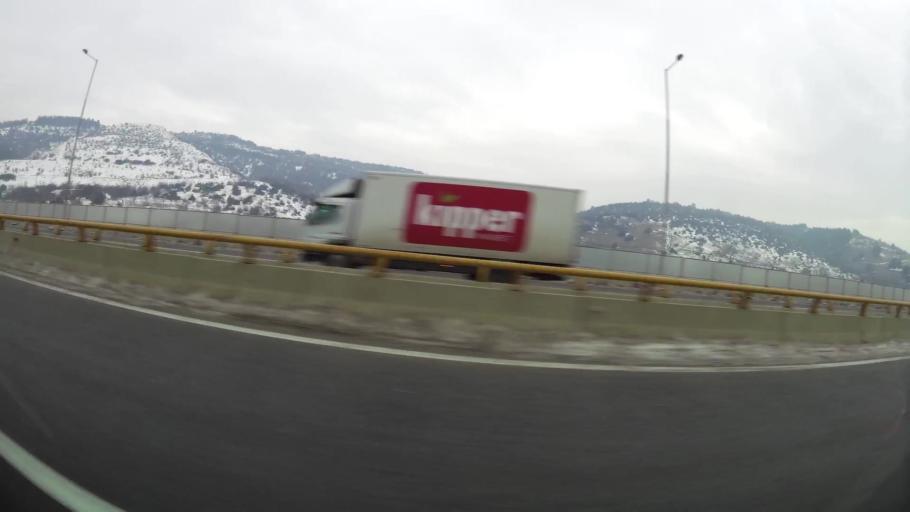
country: MK
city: Kondovo
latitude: 42.0488
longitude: 21.3380
